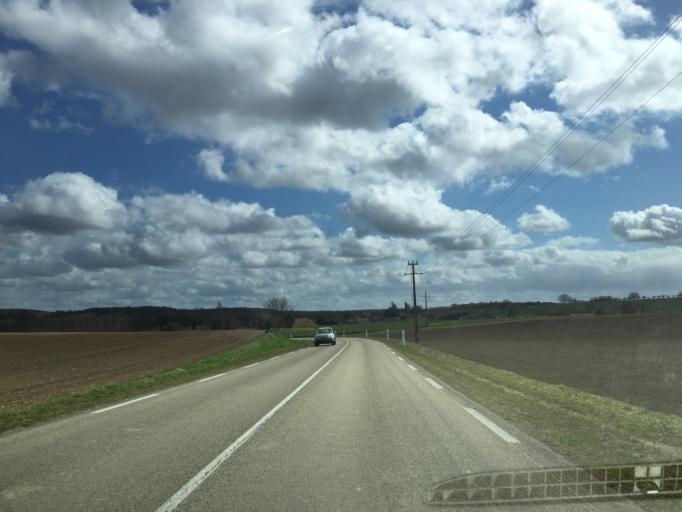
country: FR
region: Bourgogne
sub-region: Departement de l'Yonne
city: Aillant-sur-Tholon
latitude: 47.8461
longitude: 3.3868
